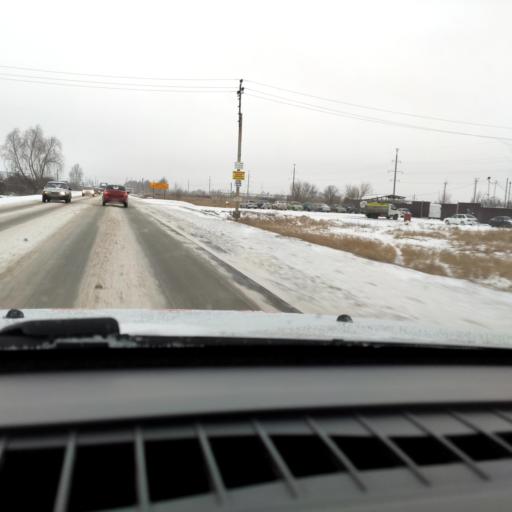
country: RU
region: Samara
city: Tol'yatti
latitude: 53.5770
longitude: 49.3381
